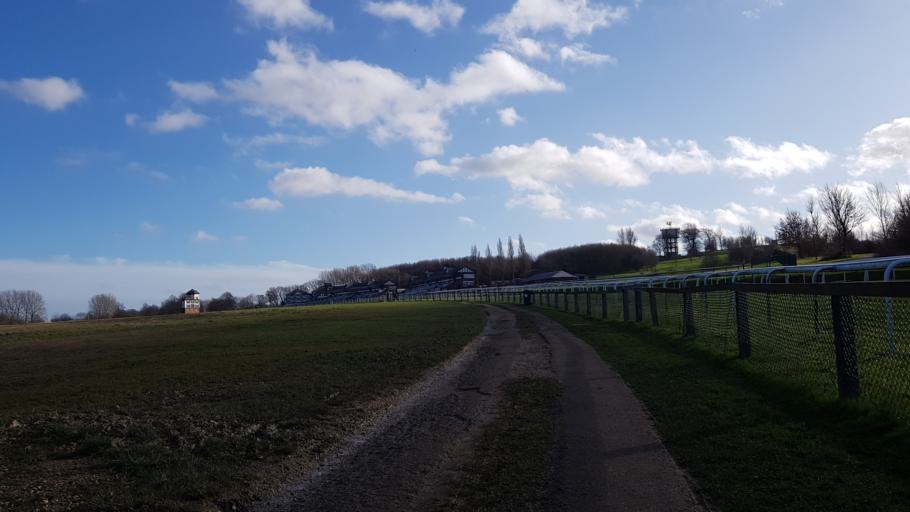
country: GB
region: England
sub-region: City and Borough of Wakefield
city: Pontefract
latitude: 53.6980
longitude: -1.3367
